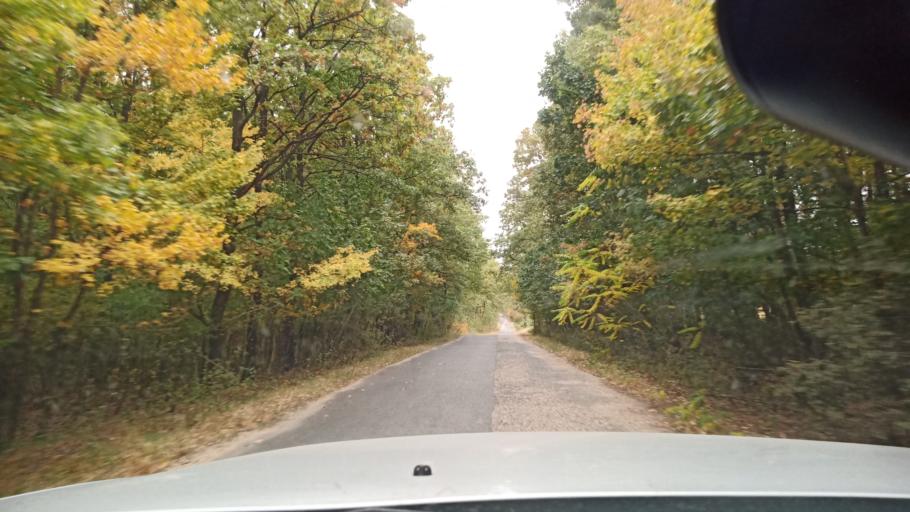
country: HU
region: Fejer
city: Zamoly
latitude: 47.3603
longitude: 18.3510
